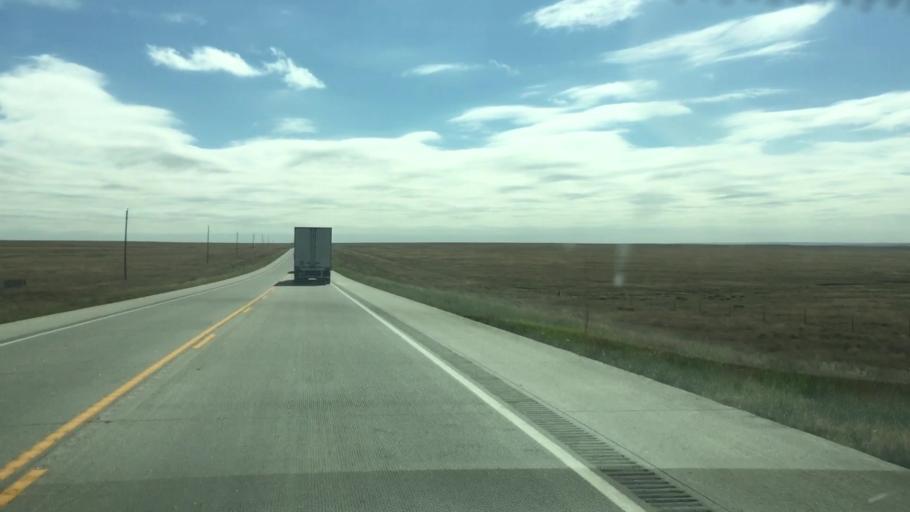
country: US
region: Colorado
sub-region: Lincoln County
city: Hugo
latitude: 39.0221
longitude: -103.3134
